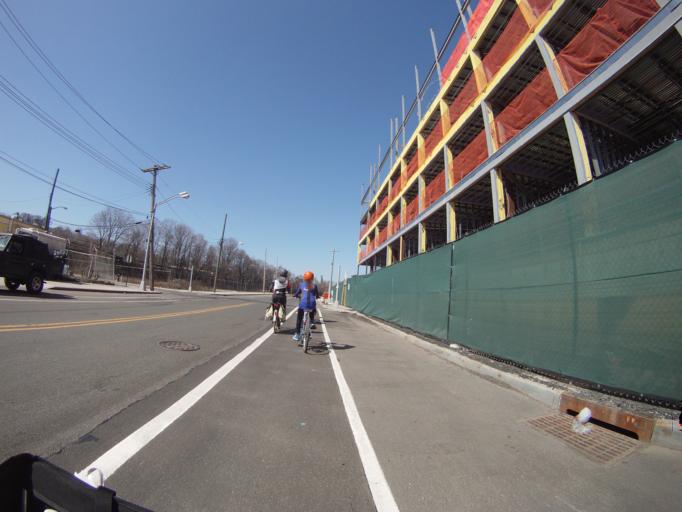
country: US
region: New Jersey
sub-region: Hudson County
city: Bayonne
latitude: 40.6295
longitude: -74.0746
